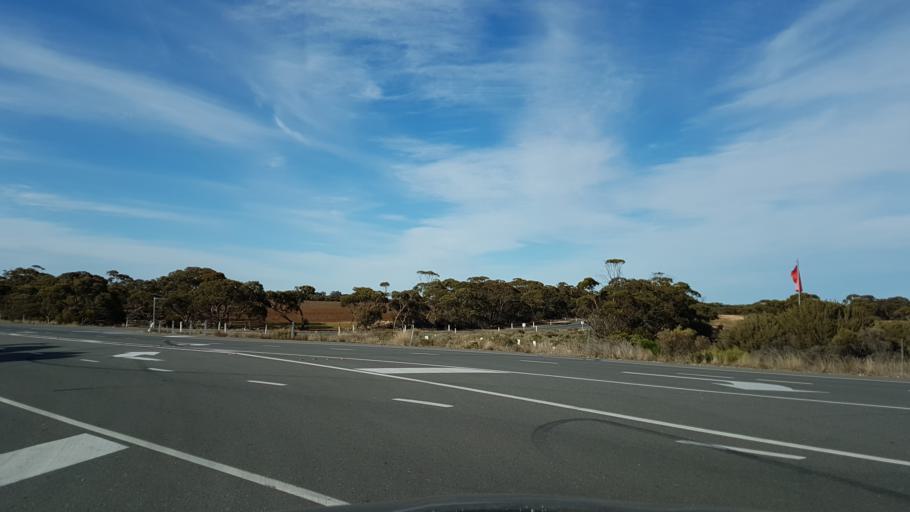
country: AU
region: South Australia
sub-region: Murray Bridge
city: Tailem Bend
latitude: -35.0874
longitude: 139.4651
